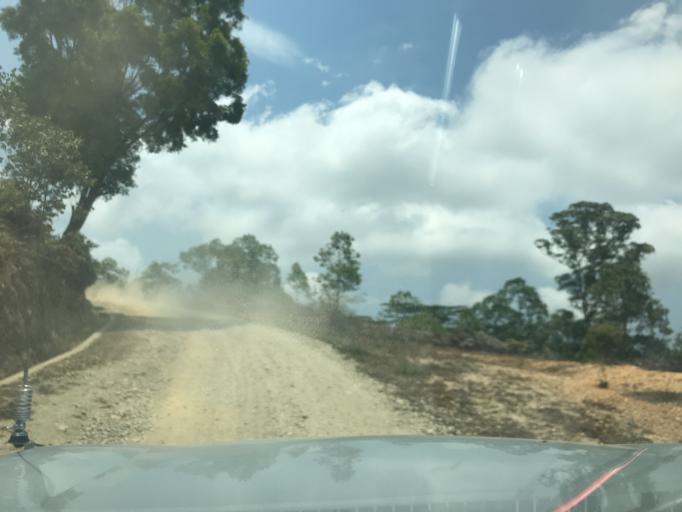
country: TL
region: Dili
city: Dili
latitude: -8.6078
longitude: 125.5866
